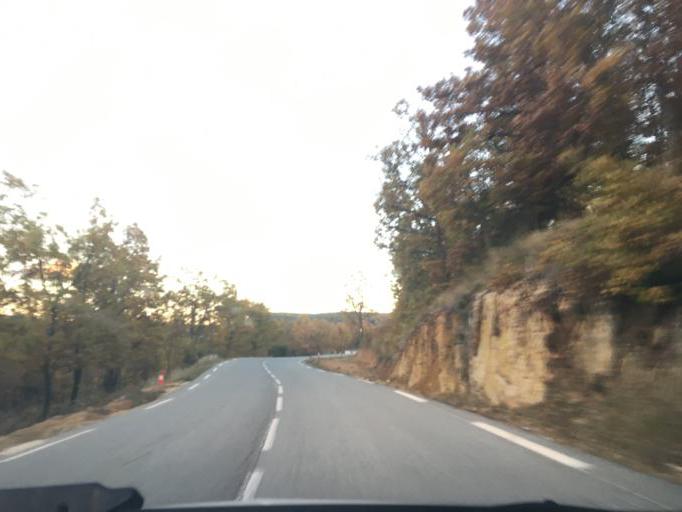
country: FR
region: Provence-Alpes-Cote d'Azur
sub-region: Departement du Var
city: Bargemon
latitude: 43.6856
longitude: 6.5096
